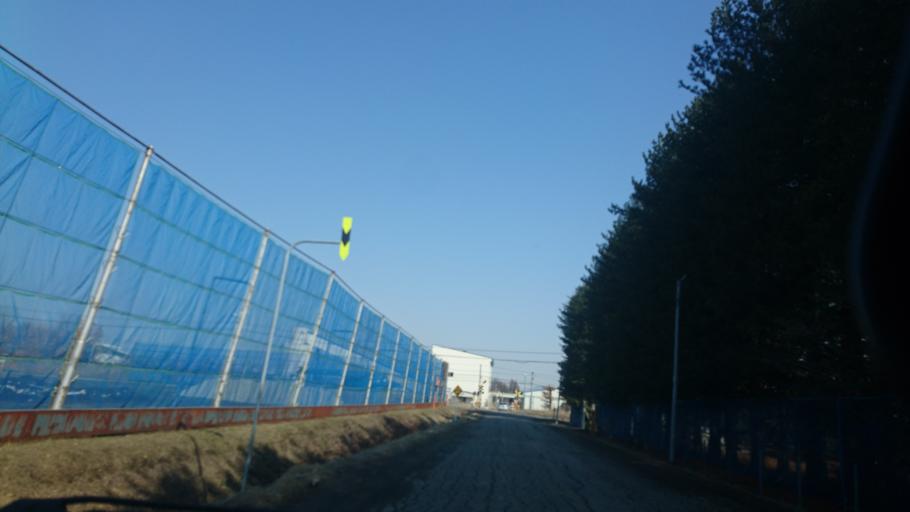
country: JP
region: Hokkaido
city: Obihiro
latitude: 42.9194
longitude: 143.0760
